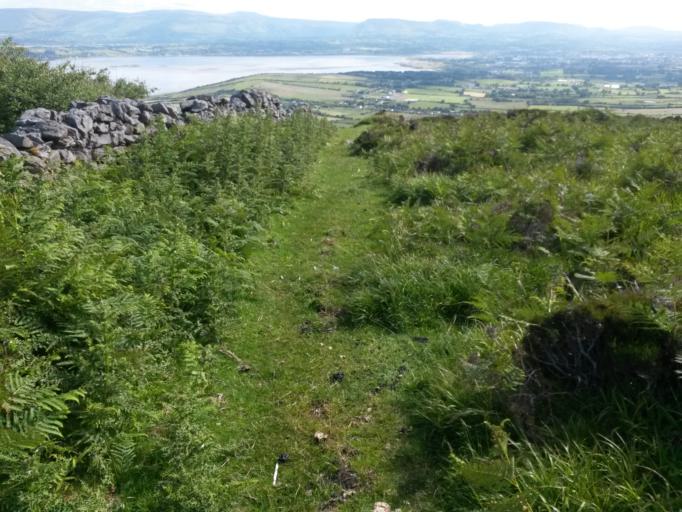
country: IE
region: Connaught
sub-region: Sligo
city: Strandhill
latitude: 54.2621
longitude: -8.5727
